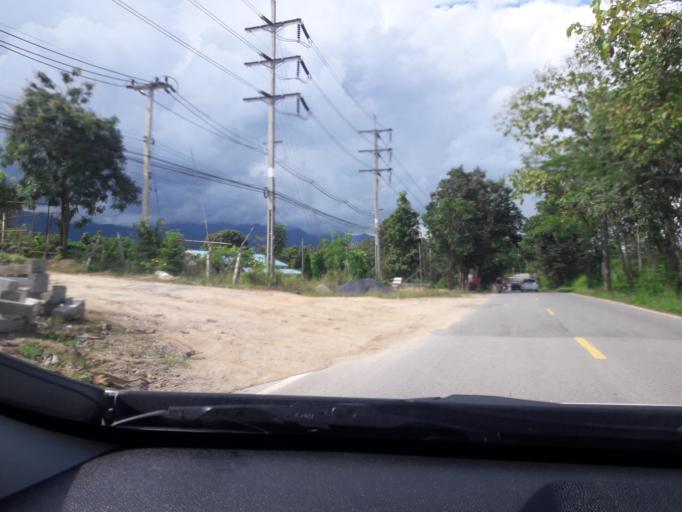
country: TH
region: Mae Hong Son
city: Mae Hi
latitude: 19.3195
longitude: 98.4380
